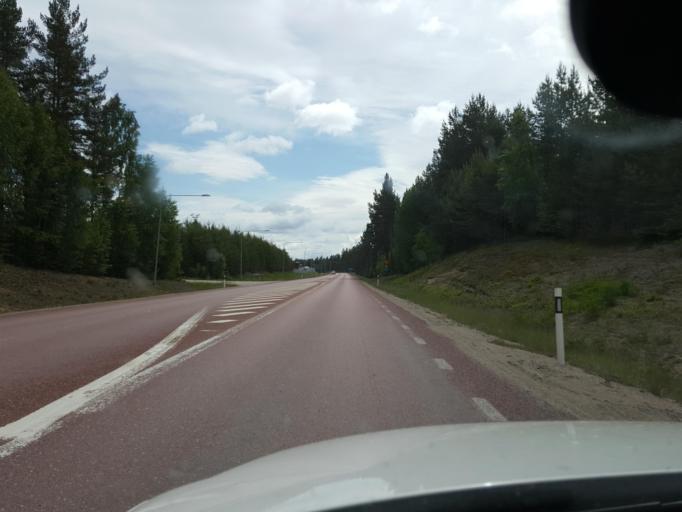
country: SE
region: Gaevleborg
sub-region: Ljusdals Kommun
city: Farila
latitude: 61.8081
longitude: 15.7752
